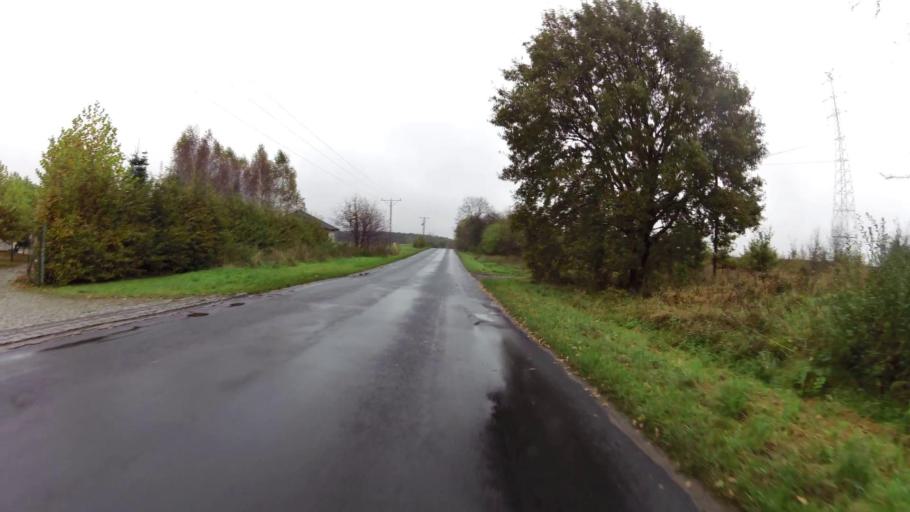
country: PL
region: West Pomeranian Voivodeship
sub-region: Powiat gryfinski
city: Gryfino
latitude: 53.2377
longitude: 14.5131
